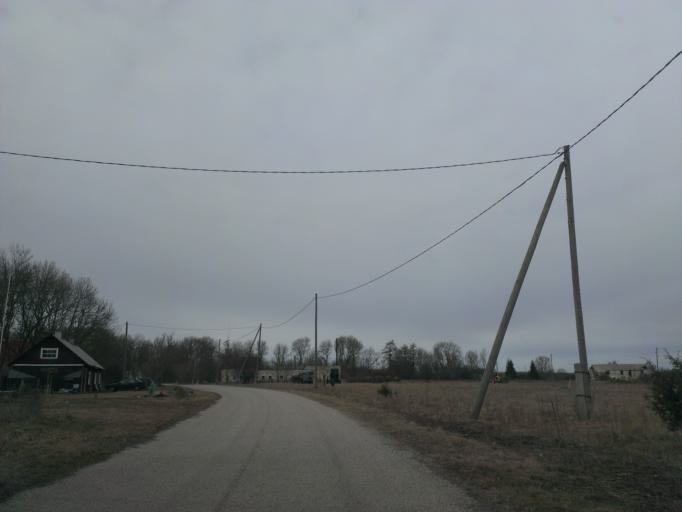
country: EE
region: Laeaene
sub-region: Lihula vald
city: Lihula
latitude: 58.5794
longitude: 23.5406
